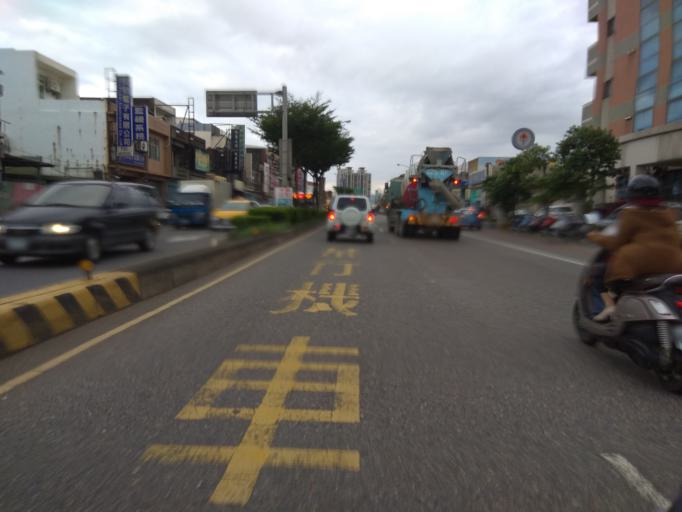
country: TW
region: Taiwan
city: Daxi
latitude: 24.9278
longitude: 121.2133
